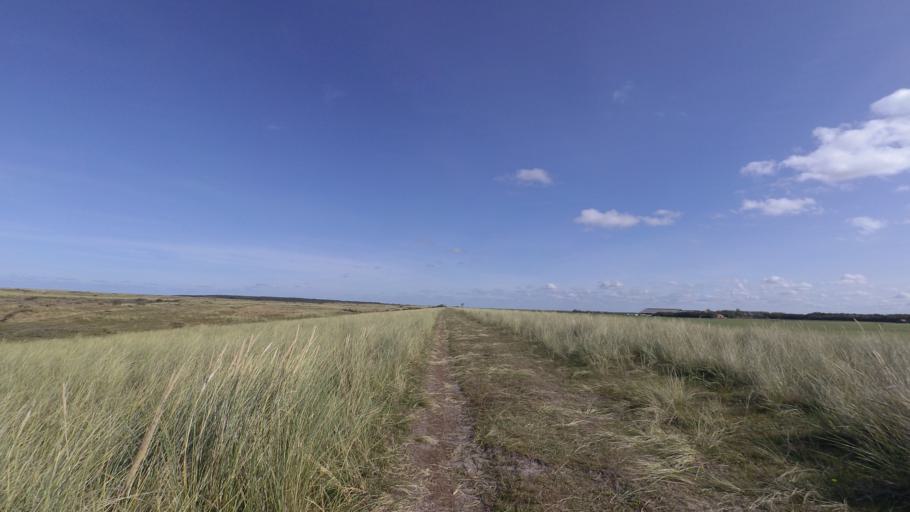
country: NL
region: Friesland
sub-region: Gemeente Ameland
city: Nes
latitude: 53.4517
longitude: 5.7199
